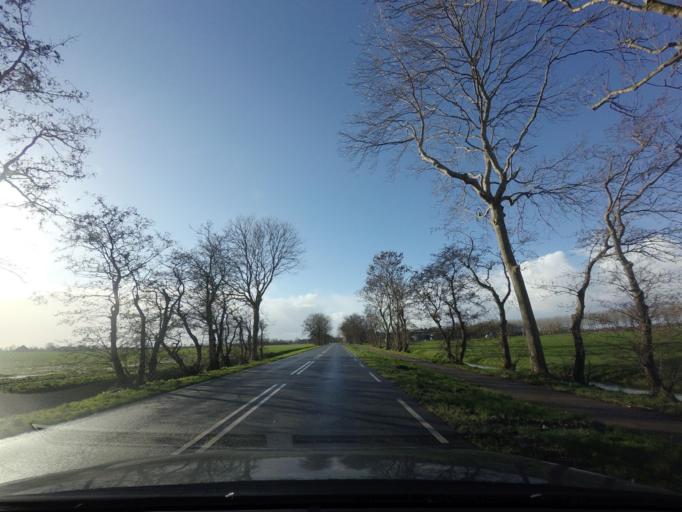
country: NL
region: North Holland
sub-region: Gemeente Opmeer
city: Opmeer
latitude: 52.7491
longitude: 4.9260
